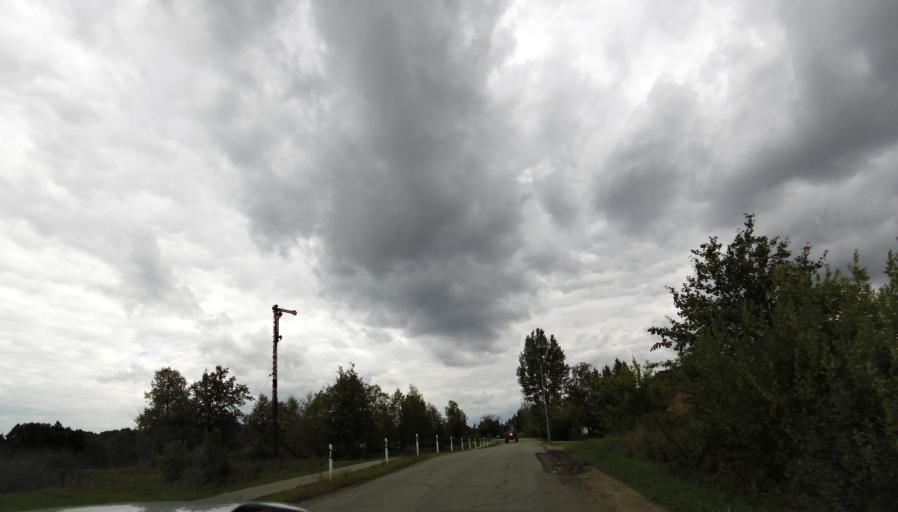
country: LT
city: Linkuva
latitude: 56.0293
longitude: 24.1662
